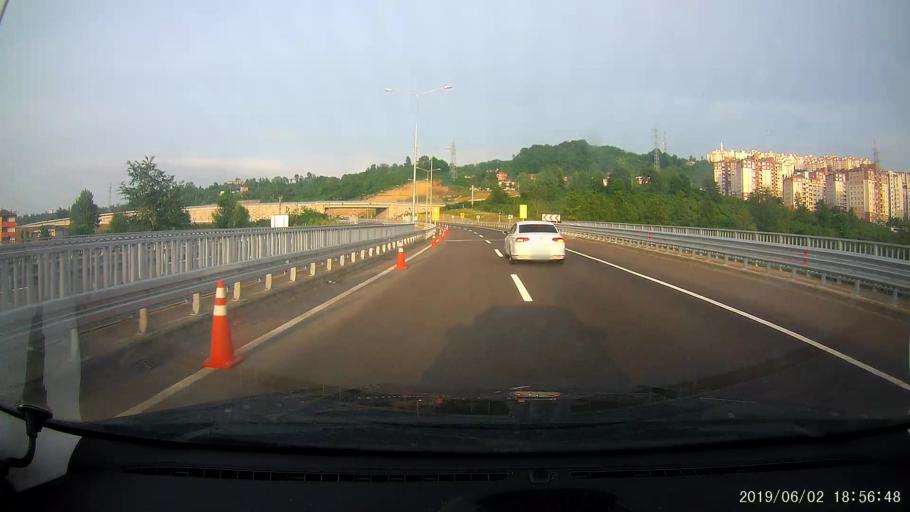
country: TR
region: Ordu
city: Ordu
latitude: 40.9537
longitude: 37.8996
